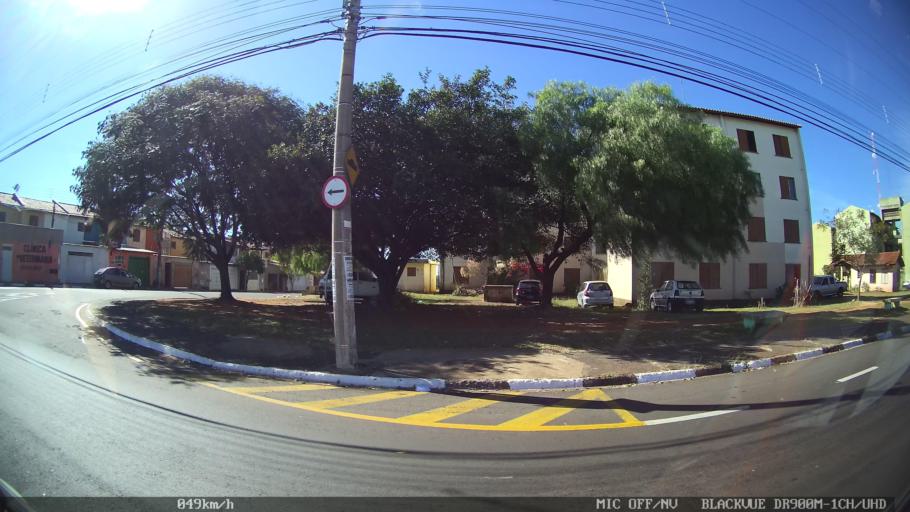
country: BR
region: Sao Paulo
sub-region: Franca
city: Franca
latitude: -20.5533
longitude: -47.3601
